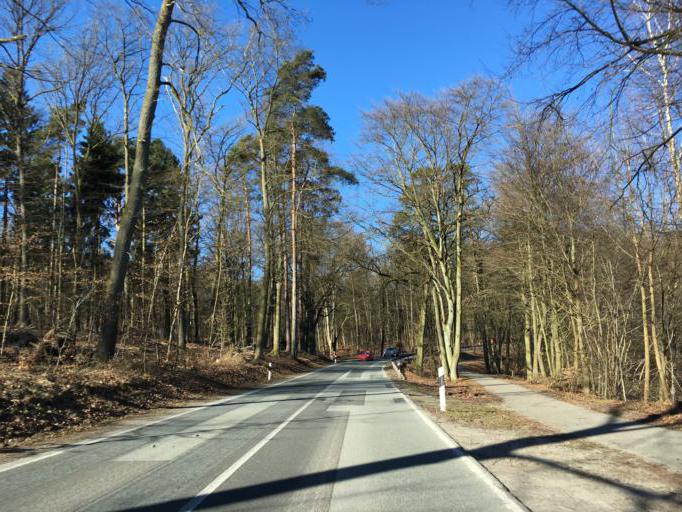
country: DE
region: Schleswig-Holstein
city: Molln
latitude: 53.6024
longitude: 10.7094
